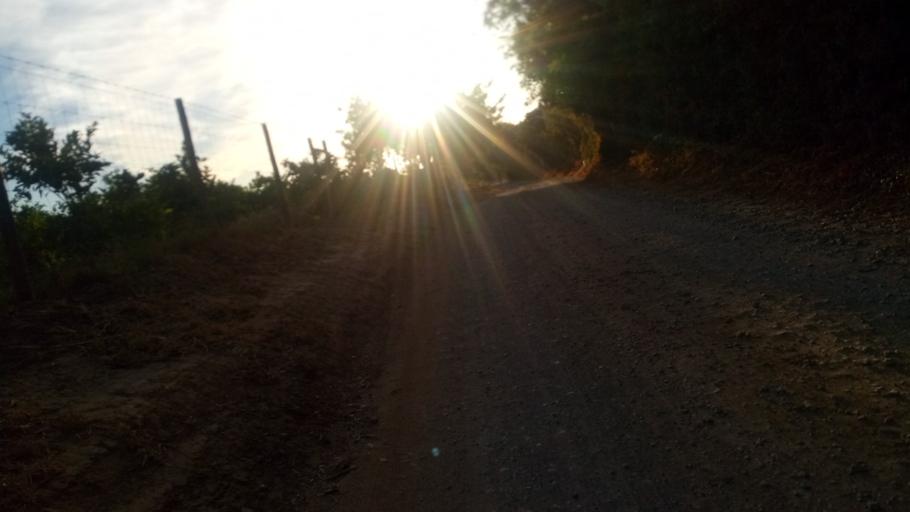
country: PT
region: Faro
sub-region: Tavira
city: Tavira
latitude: 37.1473
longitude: -7.5887
